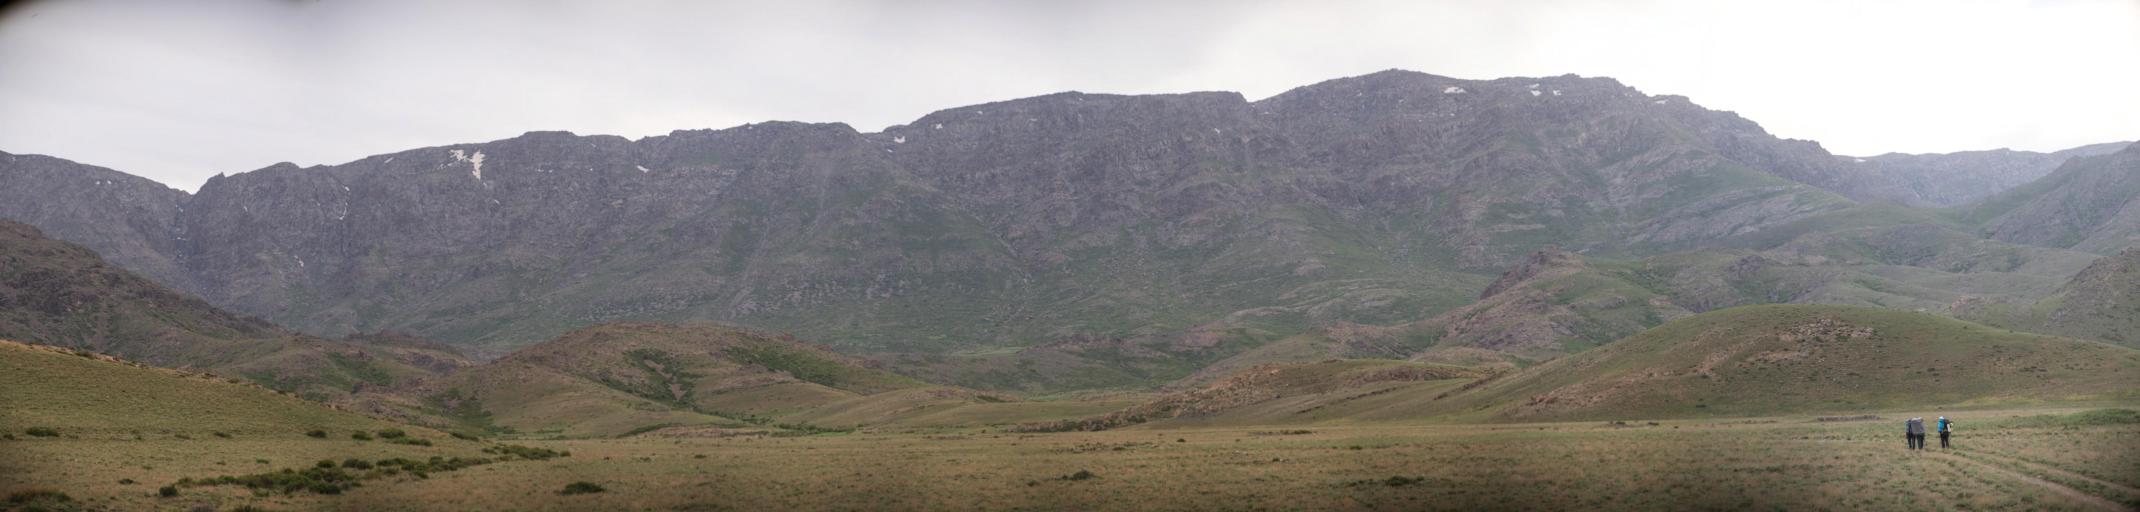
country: KZ
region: Ongtustik Qazaqstan
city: Khantaghy
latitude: 43.8882
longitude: 68.5226
